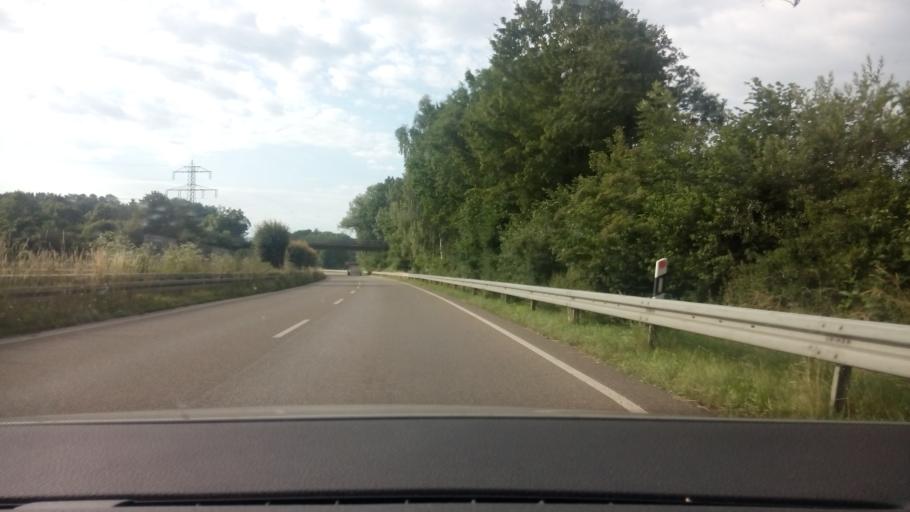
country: DE
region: Bavaria
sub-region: Upper Bavaria
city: Karlsfeld
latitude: 48.2329
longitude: 11.4530
